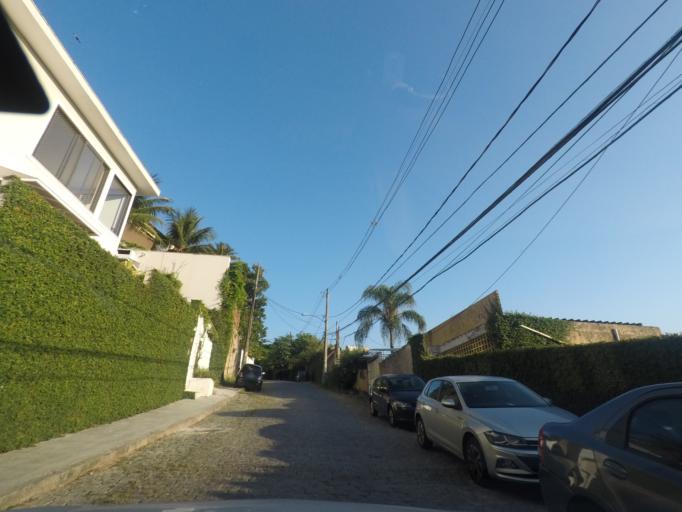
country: BR
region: Rio de Janeiro
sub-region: Rio De Janeiro
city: Rio de Janeiro
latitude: -22.9416
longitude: -43.1938
